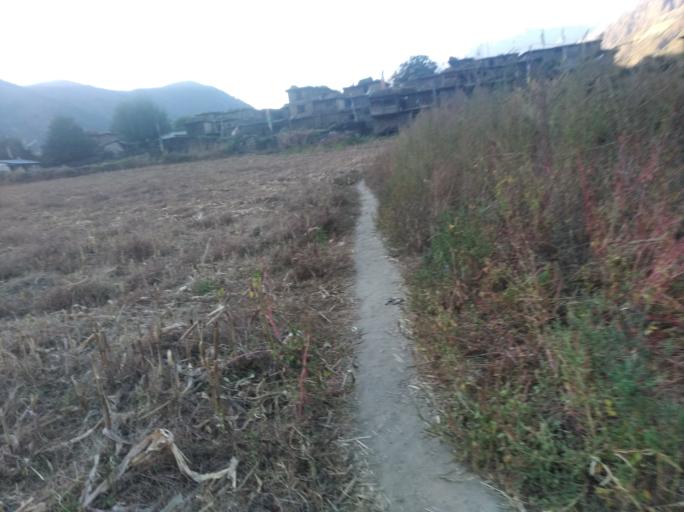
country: NP
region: Western Region
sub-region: Dhawalagiri Zone
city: Jomsom
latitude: 28.8725
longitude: 82.9937
